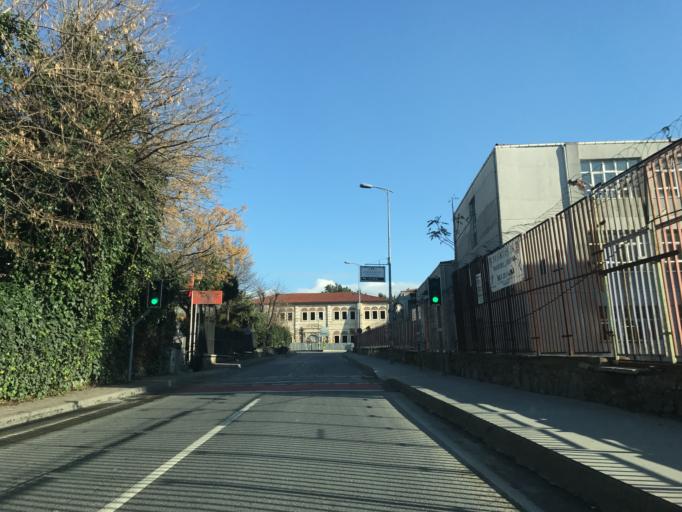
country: TR
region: Istanbul
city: Esenler
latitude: 41.0471
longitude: 28.9135
